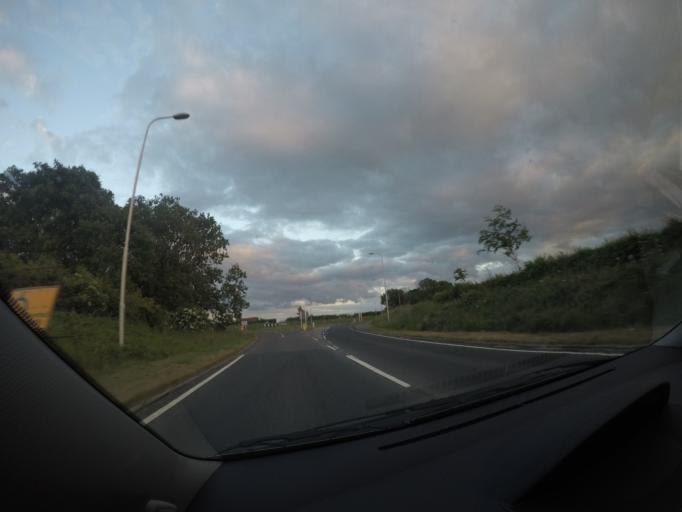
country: GB
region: England
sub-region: North Yorkshire
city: Ripon
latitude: 54.2243
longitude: -1.4890
